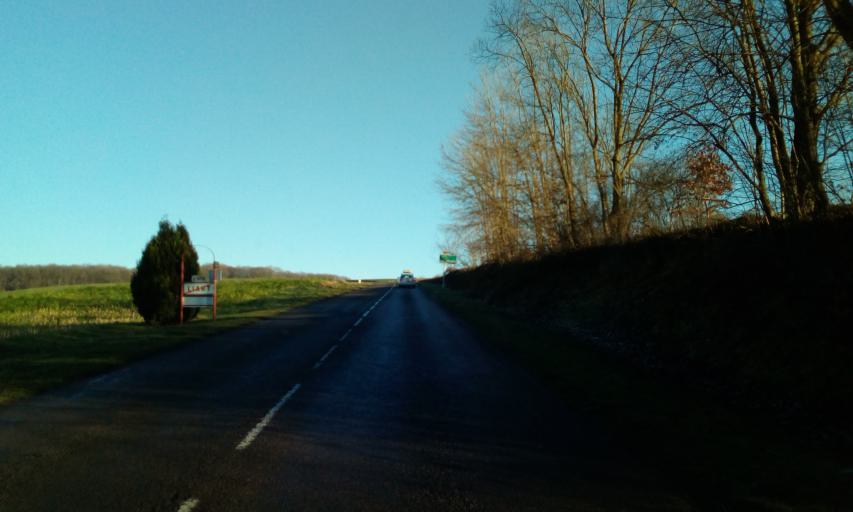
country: FR
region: Champagne-Ardenne
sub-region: Departement des Ardennes
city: Signy-le-Petit
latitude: 49.7712
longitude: 4.3473
